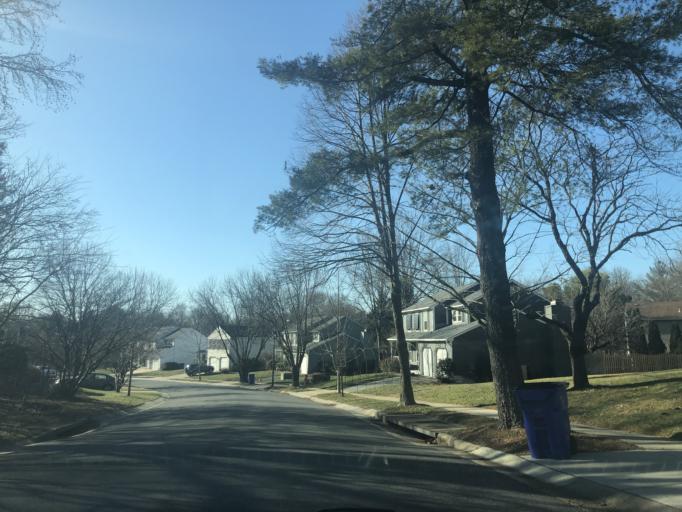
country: US
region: Maryland
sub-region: Howard County
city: Columbia
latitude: 39.2009
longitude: -76.8292
